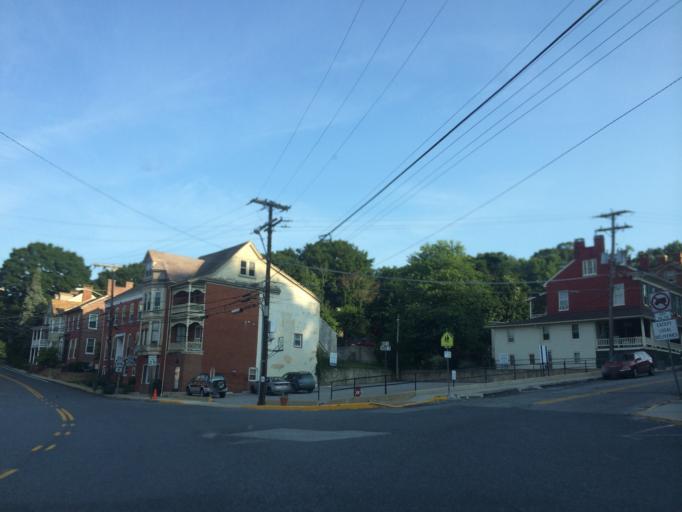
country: US
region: Pennsylvania
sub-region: York County
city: Glen Rock
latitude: 39.7945
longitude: -76.7317
